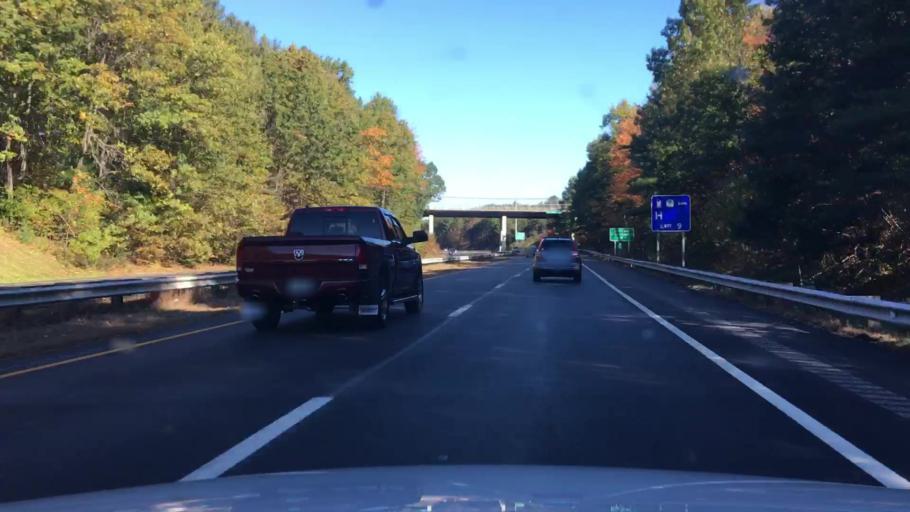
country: US
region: New Hampshire
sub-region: Strafford County
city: Dover
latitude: 43.2108
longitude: -70.8935
